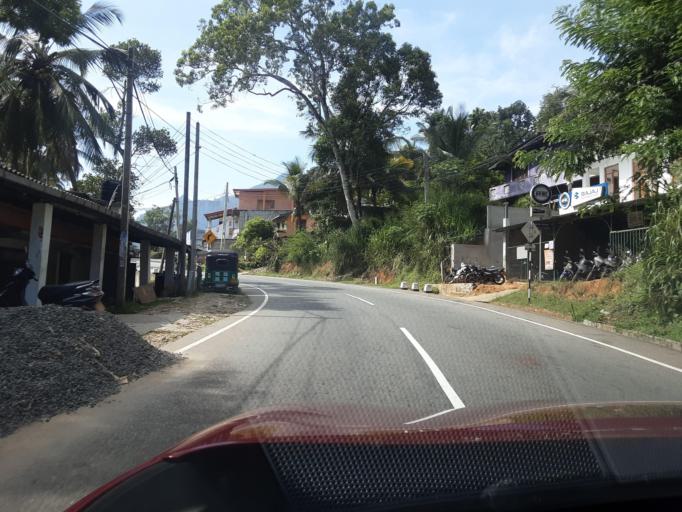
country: LK
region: Uva
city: Badulla
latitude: 6.9781
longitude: 81.0849
